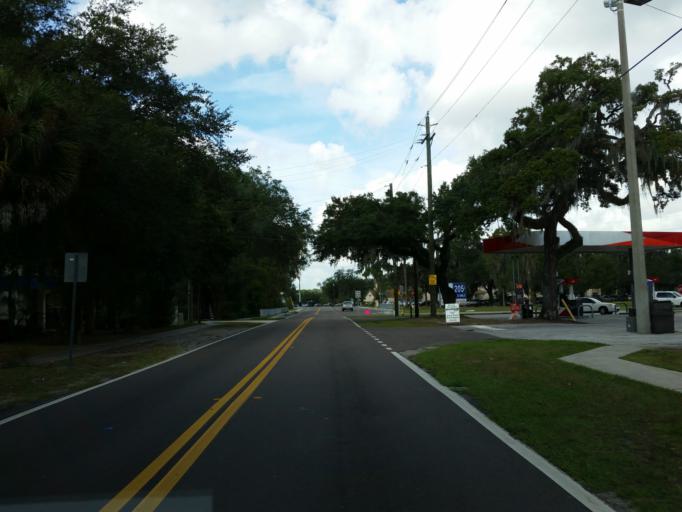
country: US
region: Florida
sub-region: Hillsborough County
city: Riverview
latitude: 27.8640
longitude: -82.3242
